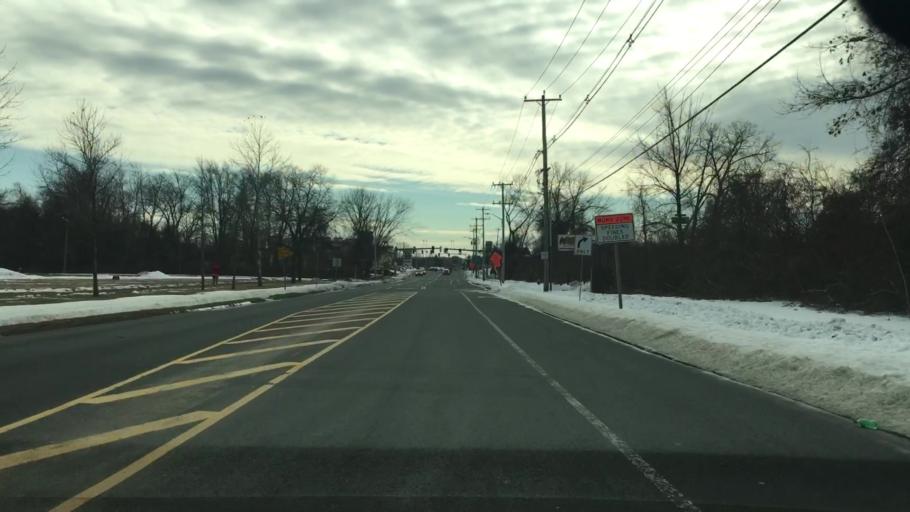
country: US
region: Massachusetts
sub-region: Hampden County
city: Holyoke
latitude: 42.1773
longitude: -72.6404
